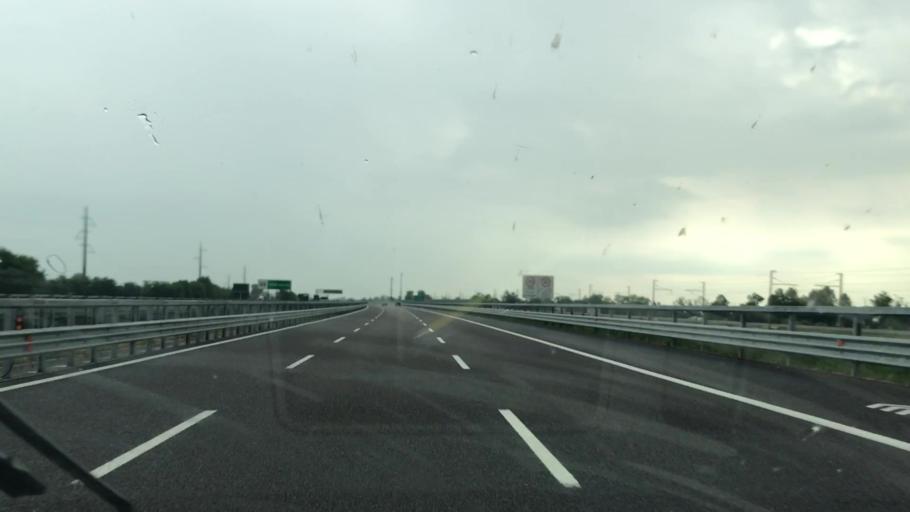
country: IT
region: Lombardy
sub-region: Provincia di Bergamo
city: Calcio
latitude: 45.4952
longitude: 9.8392
